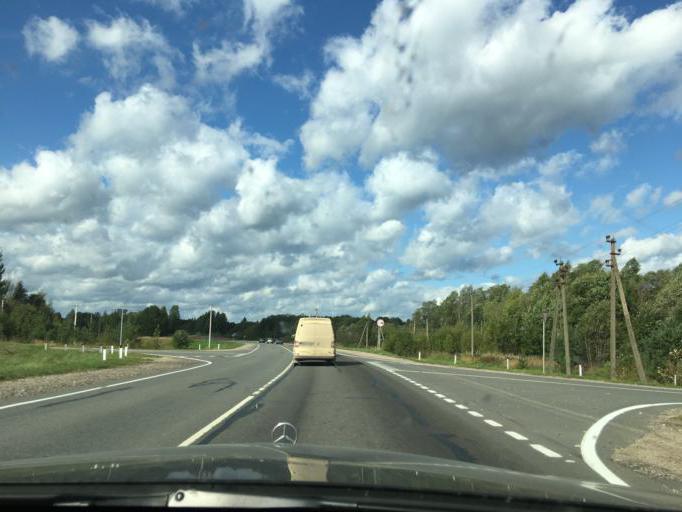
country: RU
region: Pskov
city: Pustoshka
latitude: 56.3979
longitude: 29.2373
